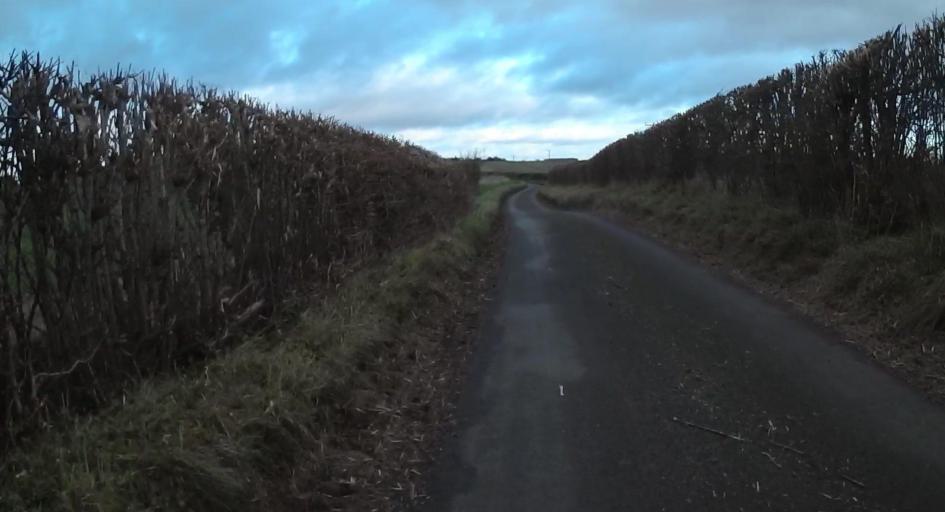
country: GB
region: England
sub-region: Hampshire
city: Long Sutton
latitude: 51.2286
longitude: -0.8803
